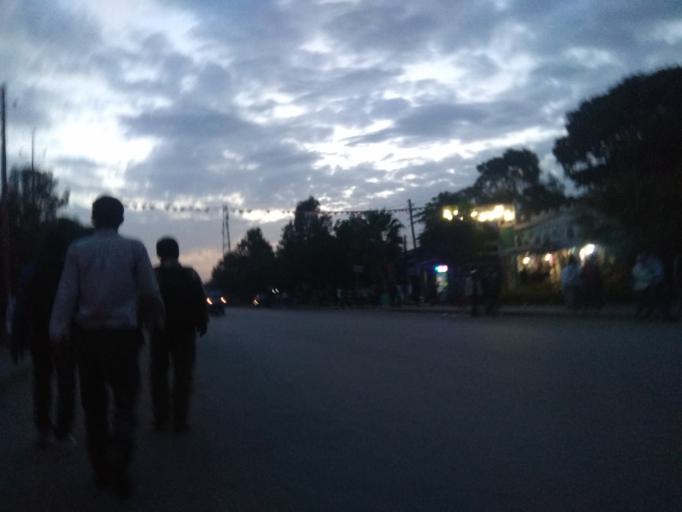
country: ET
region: Oromiya
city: Hagere Hiywet
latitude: 8.9820
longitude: 37.8542
